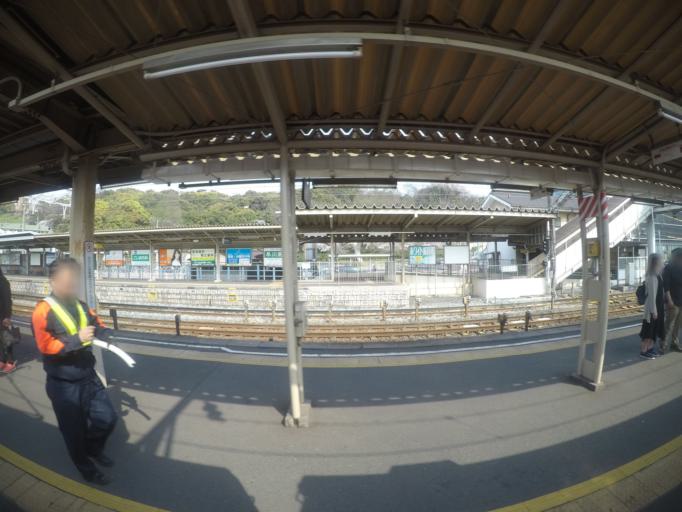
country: JP
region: Aichi
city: Obu
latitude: 35.0424
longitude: 136.9030
